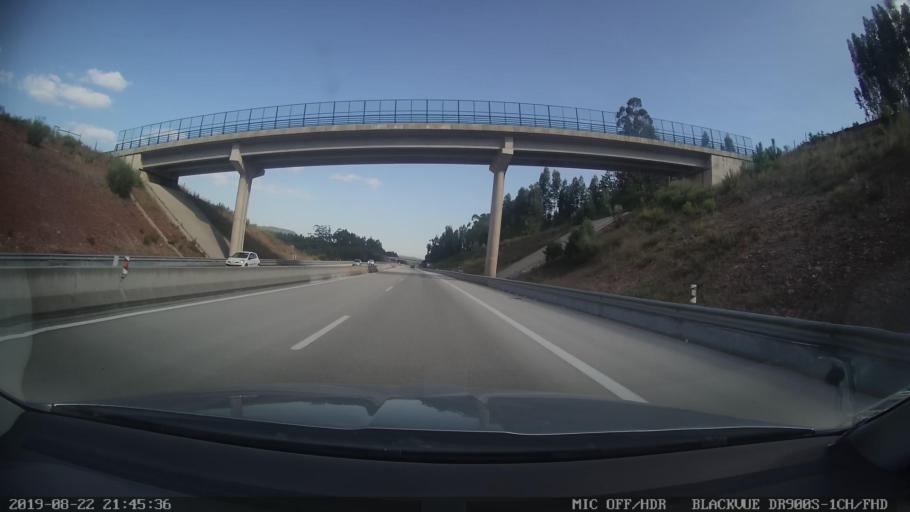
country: PT
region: Coimbra
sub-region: Penela
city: Penela
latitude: 39.9726
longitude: -8.3535
